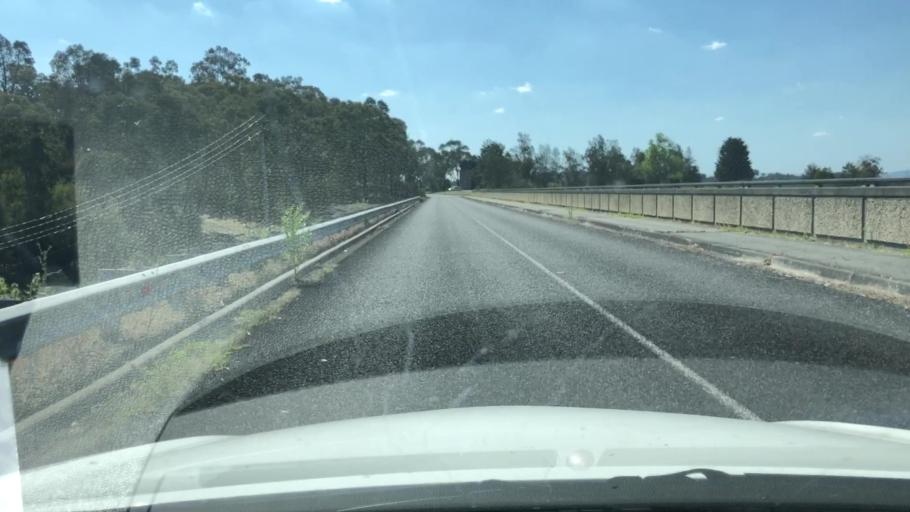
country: AU
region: Victoria
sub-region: Yarra Ranges
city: Chirnside Park
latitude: -37.6801
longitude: 145.2991
